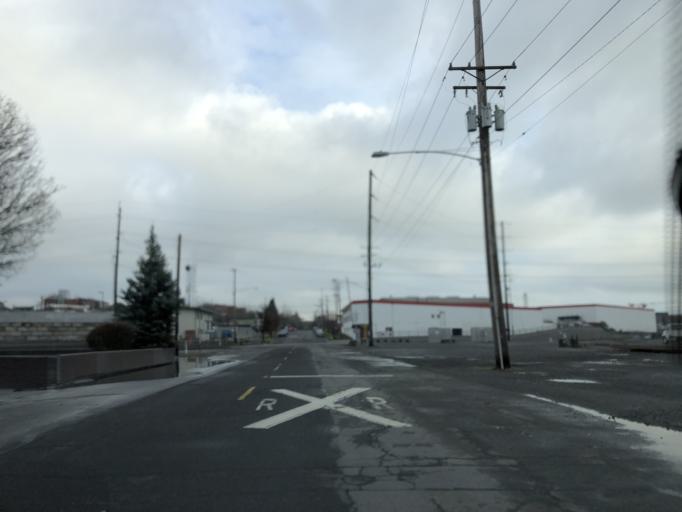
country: US
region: Washington
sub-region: Clark County
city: Vancouver
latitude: 45.6296
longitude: -122.6851
